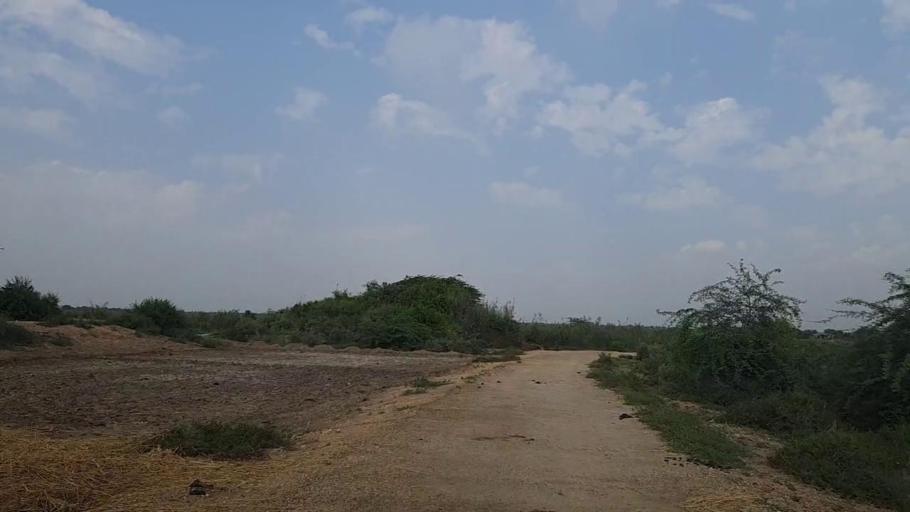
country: PK
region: Sindh
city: Daro Mehar
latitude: 24.6954
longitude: 68.1198
